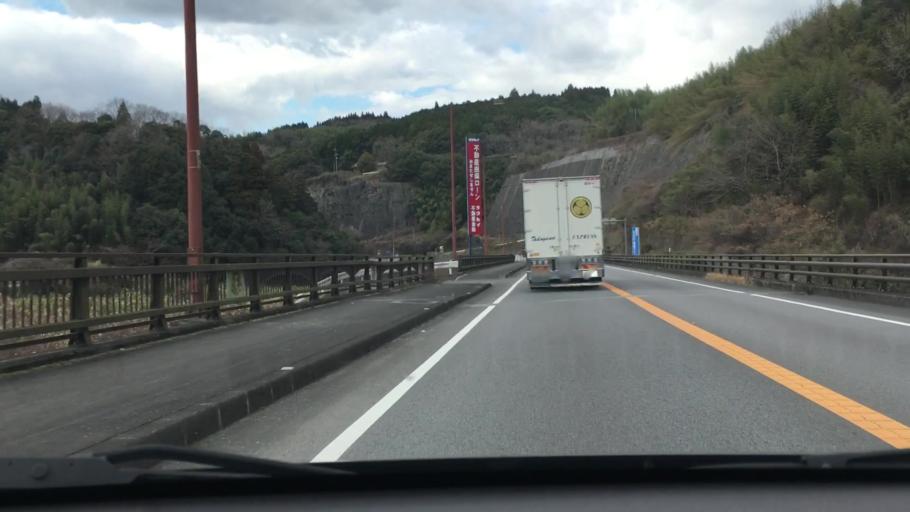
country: JP
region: Oita
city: Usuki
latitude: 33.0670
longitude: 131.6561
